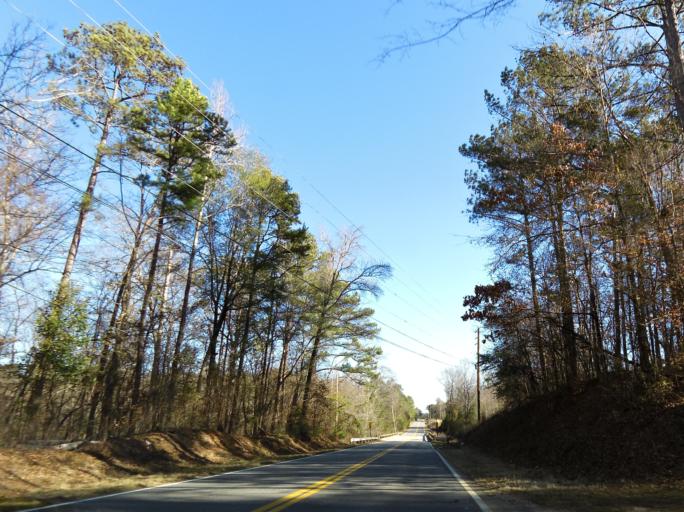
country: US
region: Georgia
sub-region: Bibb County
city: West Point
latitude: 32.7963
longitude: -83.7559
